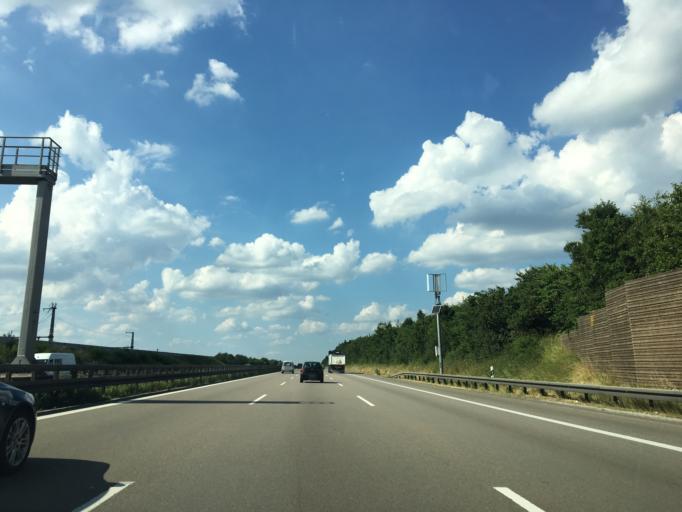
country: DE
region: Bavaria
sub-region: Regierungsbezirk Mittelfranken
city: Allersberg
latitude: 49.2633
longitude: 11.2132
